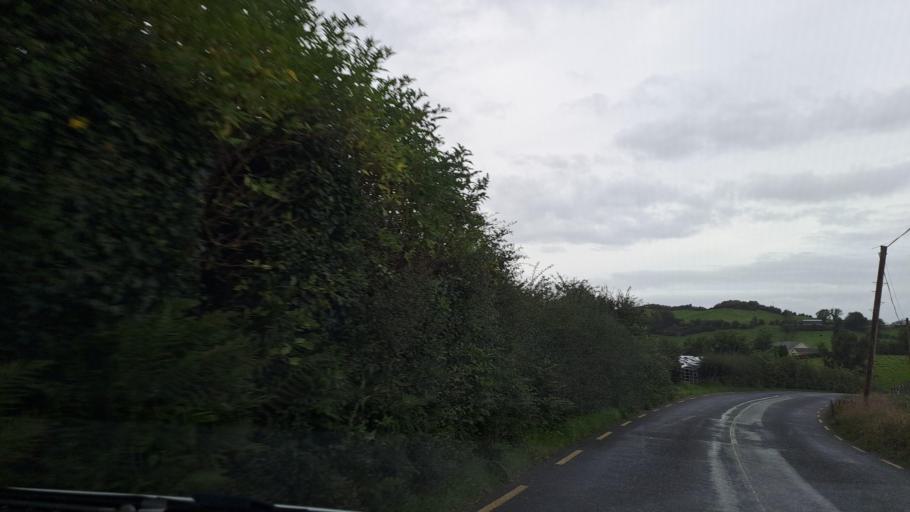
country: IE
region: Ulster
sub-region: An Cabhan
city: Bailieborough
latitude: 54.0128
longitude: -6.9097
